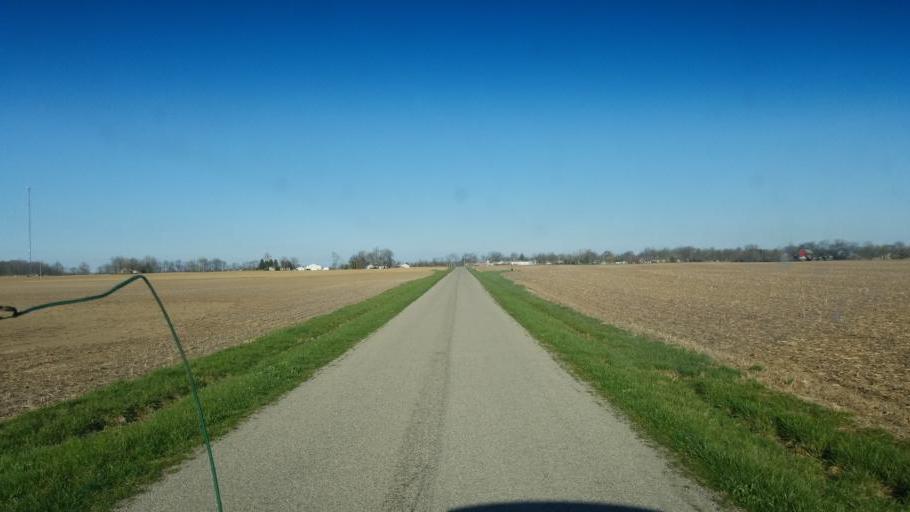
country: US
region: Ohio
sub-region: Union County
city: Richwood
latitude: 40.4510
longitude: -83.4431
